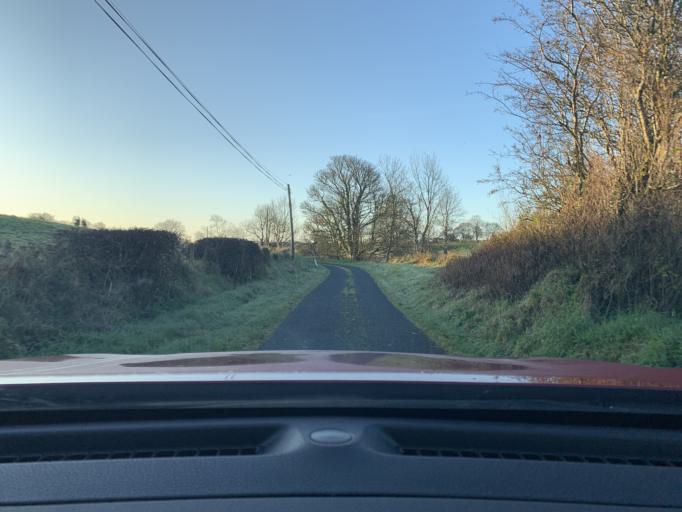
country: IE
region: Connaught
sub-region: Sligo
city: Ballymote
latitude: 54.0730
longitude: -8.5503
